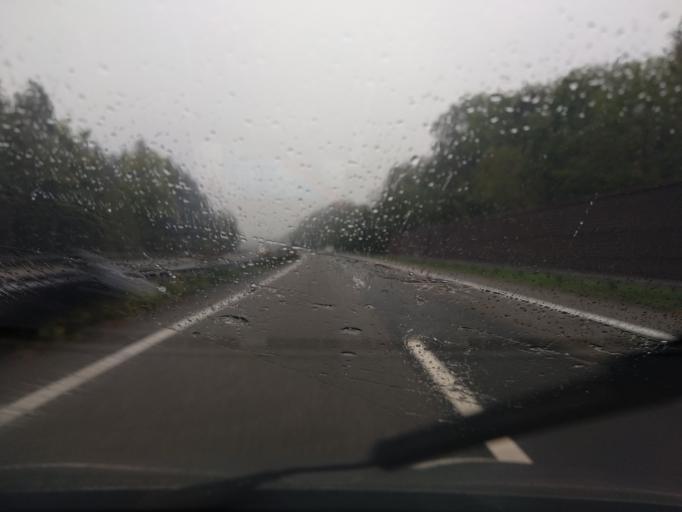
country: CH
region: Saint Gallen
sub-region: Wahlkreis Wil
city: Zuzwil
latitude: 47.4579
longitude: 9.1212
